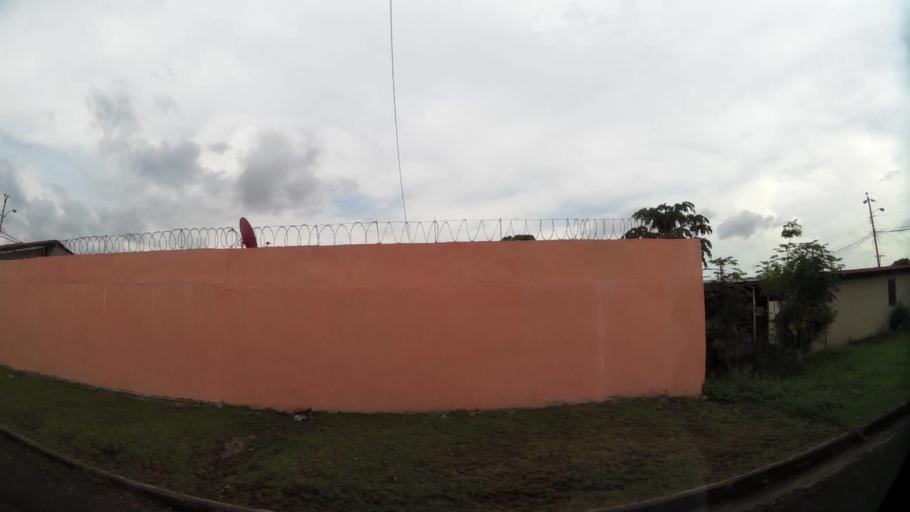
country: PA
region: Panama
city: Cabra Numero Uno
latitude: 9.0966
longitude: -79.3470
